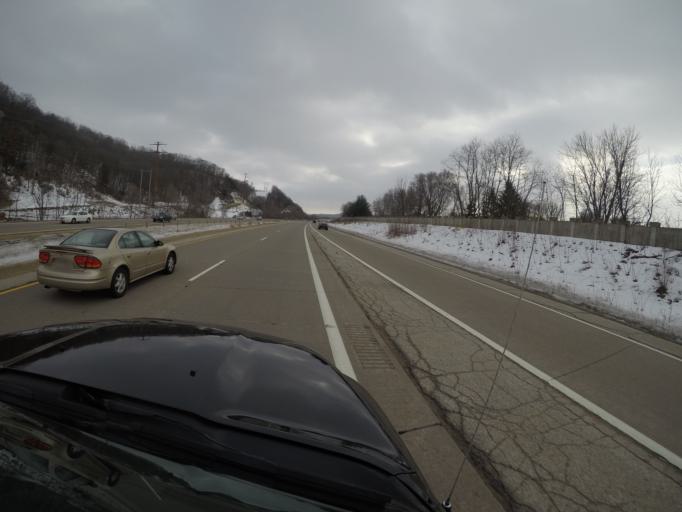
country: US
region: Wisconsin
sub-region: La Crosse County
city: Onalaska
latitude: 43.8943
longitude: -91.2169
